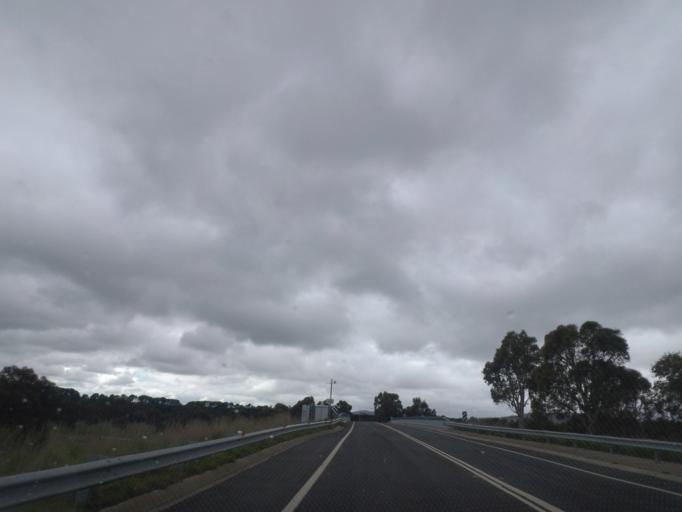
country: AU
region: Victoria
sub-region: Hume
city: Sunbury
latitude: -37.3211
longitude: 144.5256
